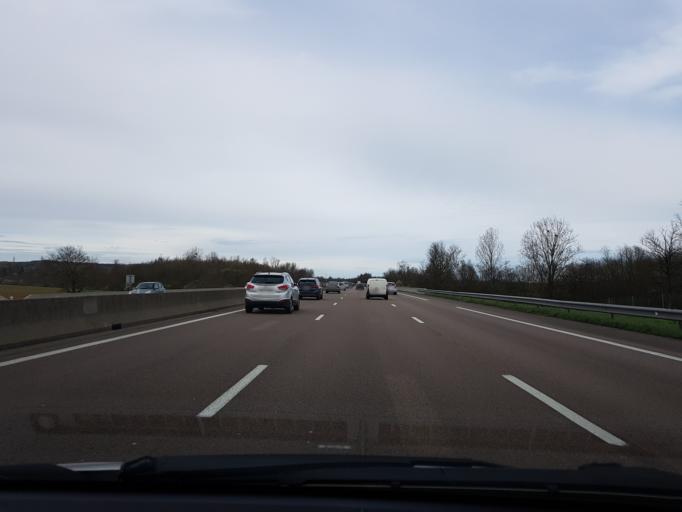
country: FR
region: Rhone-Alpes
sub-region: Departement de l'Ain
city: Pont-de-Vaux
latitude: 46.4841
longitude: 4.8919
